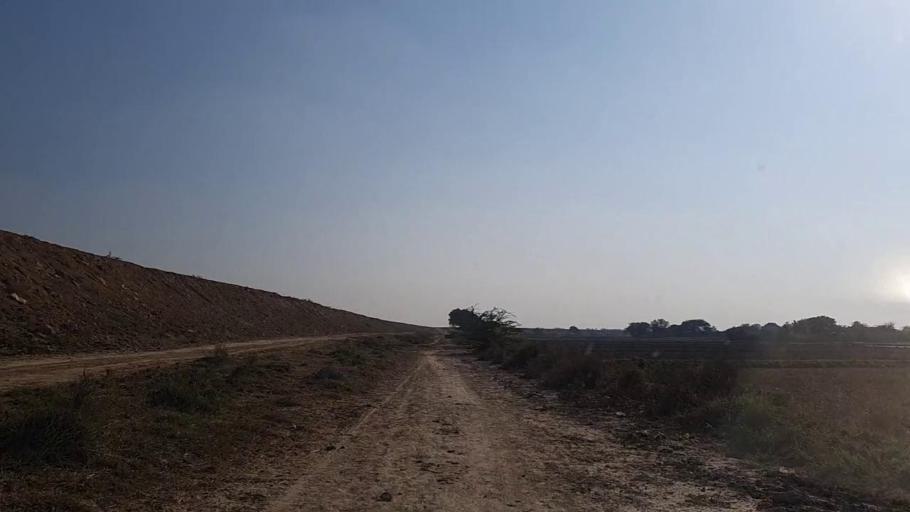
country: PK
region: Sindh
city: Thatta
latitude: 24.7287
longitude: 67.9685
